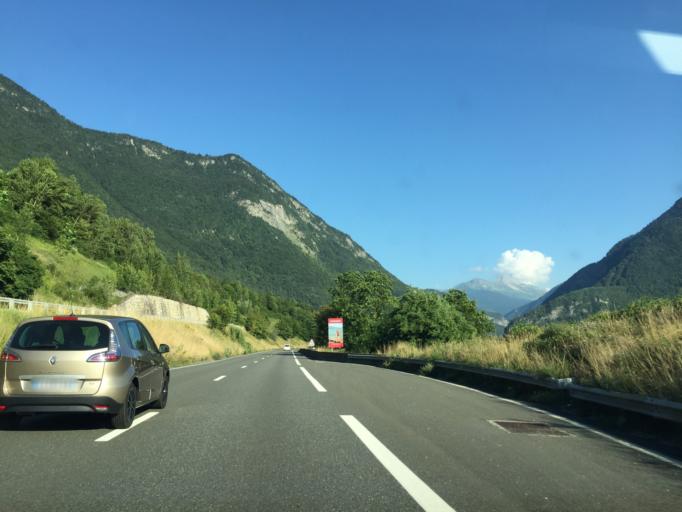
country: FR
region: Rhone-Alpes
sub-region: Departement de la Savoie
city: Aigueblanche
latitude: 45.5127
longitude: 6.4977
